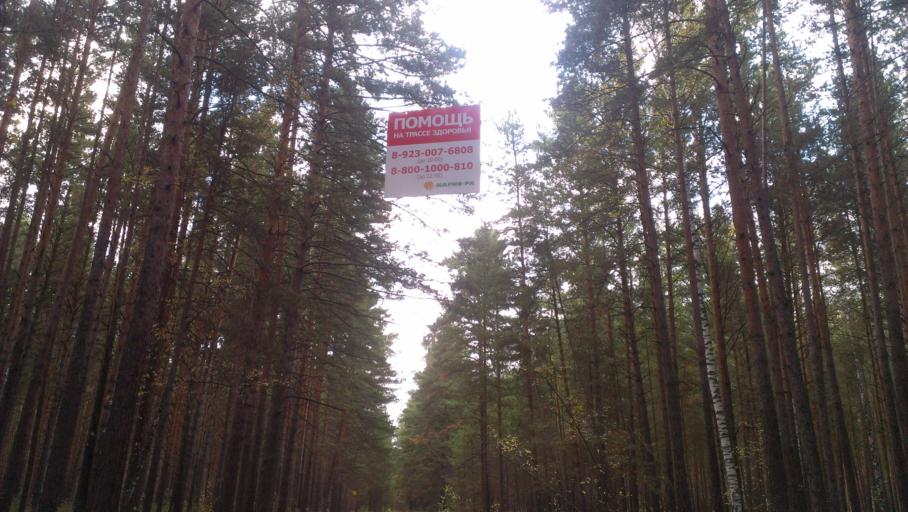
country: RU
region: Altai Krai
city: Yuzhnyy
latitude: 53.2808
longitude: 83.6991
